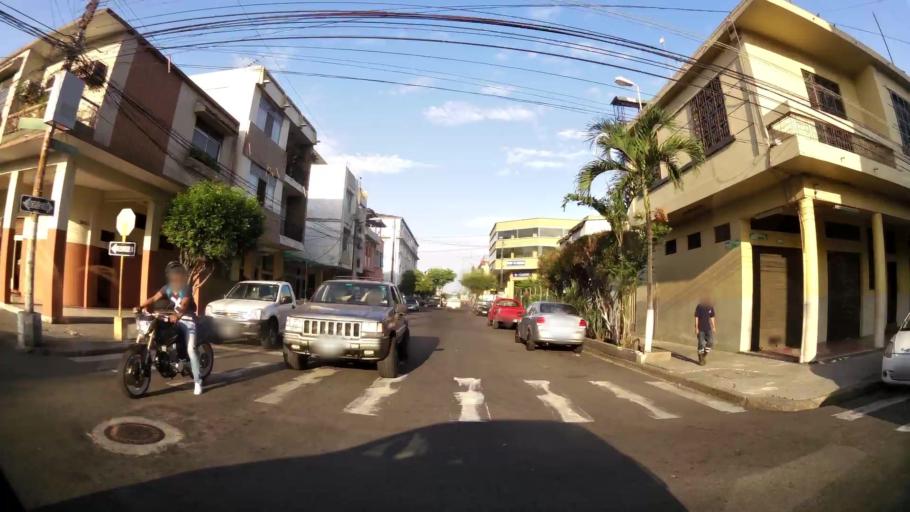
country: EC
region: Guayas
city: Guayaquil
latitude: -2.2139
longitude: -79.8886
